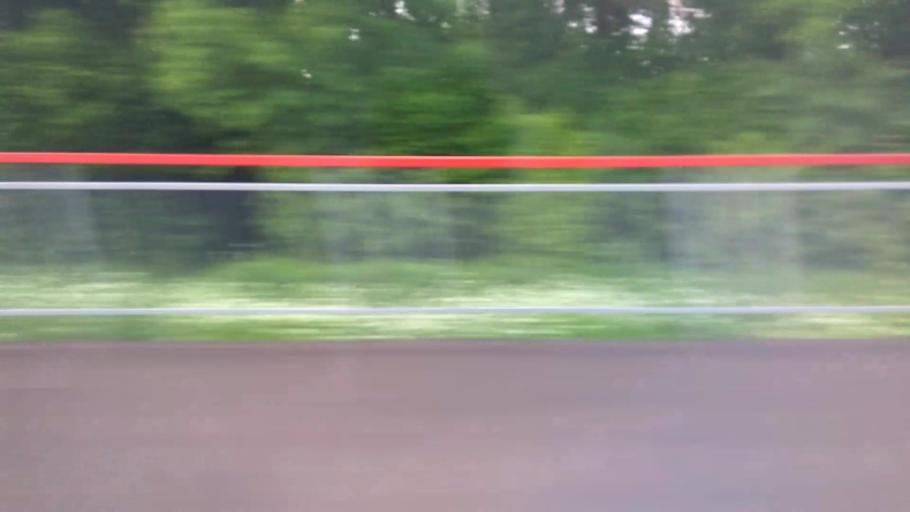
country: RU
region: Moskovskaya
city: Belyye Stolby
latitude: 55.3110
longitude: 37.8706
